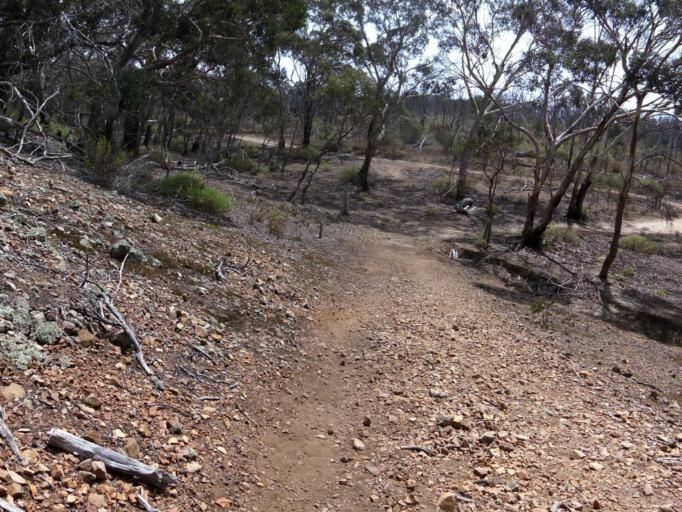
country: AU
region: Victoria
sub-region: Moorabool
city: Bacchus Marsh
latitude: -37.6599
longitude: 144.3607
